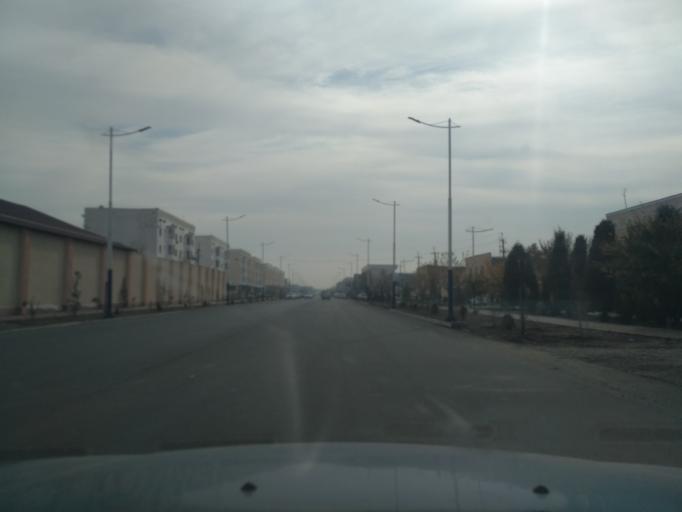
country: UZ
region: Sirdaryo
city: Guliston
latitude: 40.5090
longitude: 68.7695
